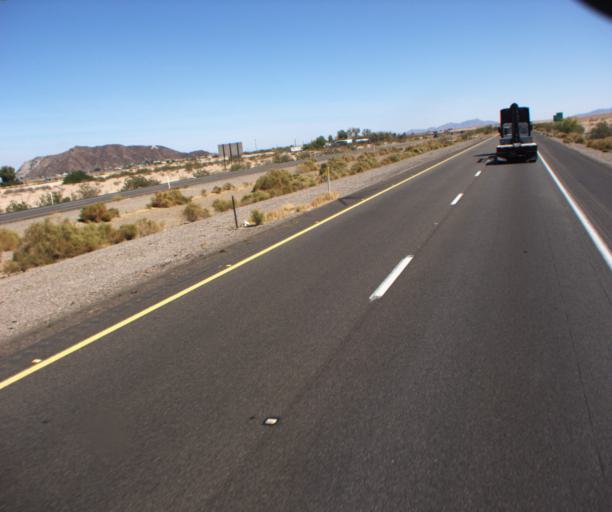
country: US
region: Arizona
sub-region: Yuma County
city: Wellton
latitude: 32.6780
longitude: -114.0383
